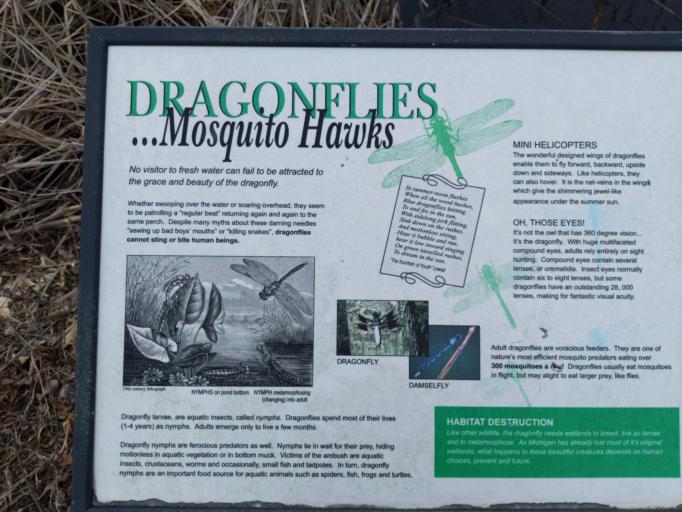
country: US
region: Michigan
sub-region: Bay County
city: Bay City
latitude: 43.6783
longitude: -83.9192
